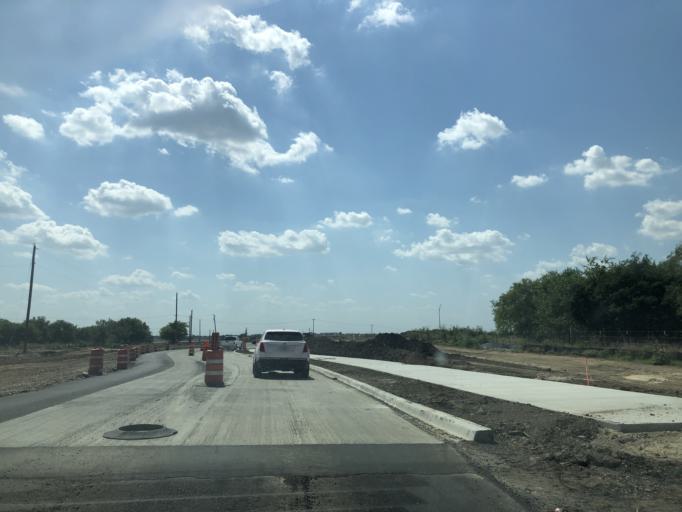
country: US
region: Texas
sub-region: Tarrant County
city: Haslet
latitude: 32.9243
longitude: -97.3529
